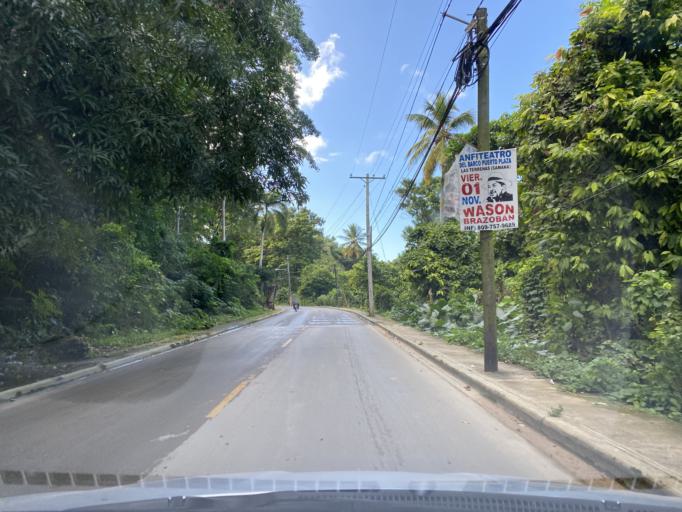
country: DO
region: Samana
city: Las Terrenas
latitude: 19.3064
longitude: -69.5582
